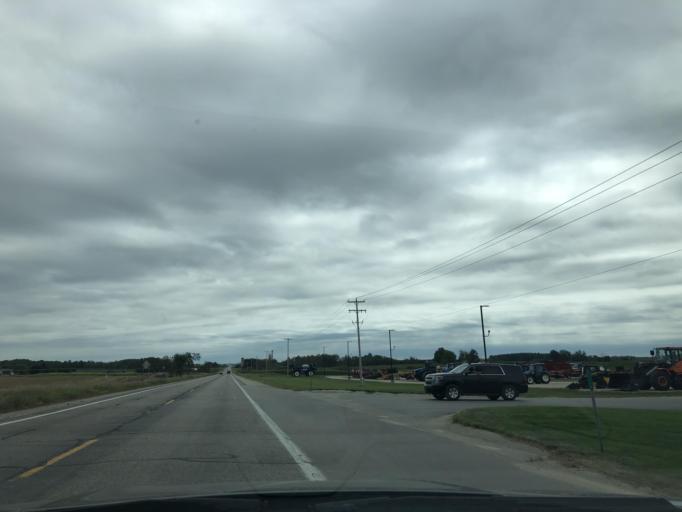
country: US
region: Michigan
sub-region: Missaukee County
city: Lake City
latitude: 44.1937
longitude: -85.1995
